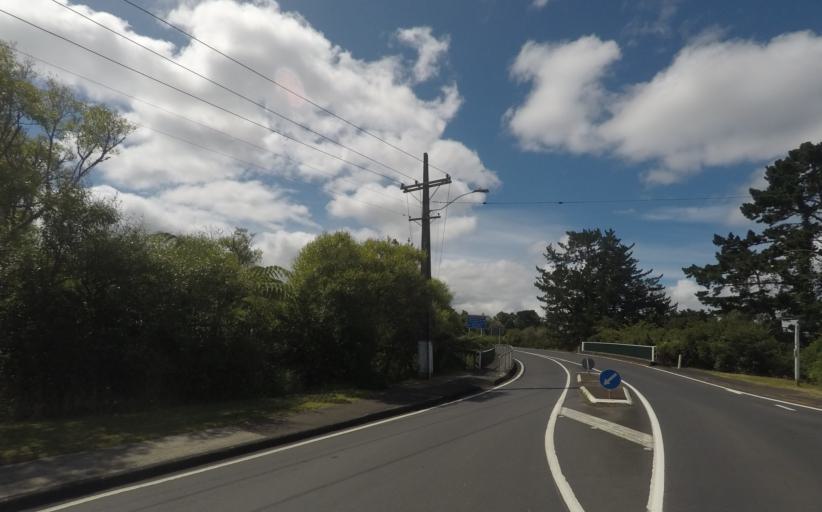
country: NZ
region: Auckland
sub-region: Auckland
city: Muriwai Beach
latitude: -36.8505
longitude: 174.5425
